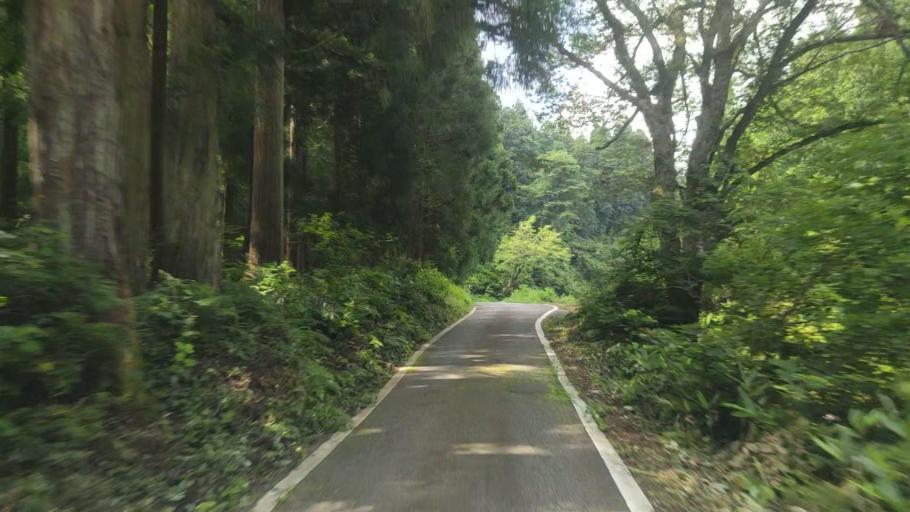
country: JP
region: Fukui
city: Katsuyama
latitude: 36.1913
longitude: 136.5258
